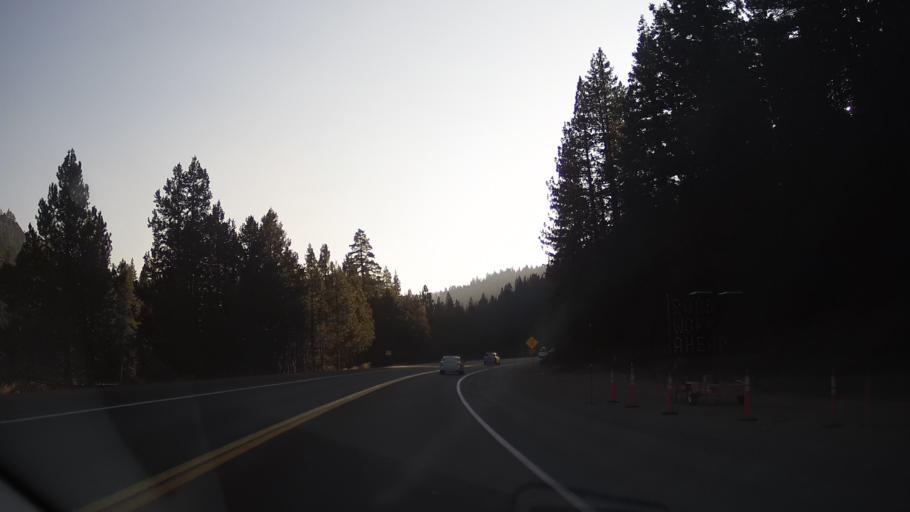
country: US
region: California
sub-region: Nevada County
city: Truckee
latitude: 39.2693
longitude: -120.2080
